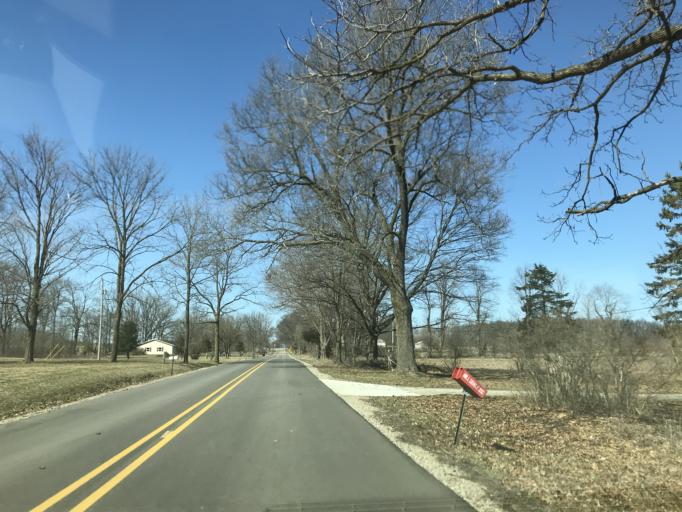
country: US
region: Michigan
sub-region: Hillsdale County
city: Jonesville
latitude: 41.9855
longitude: -84.6777
